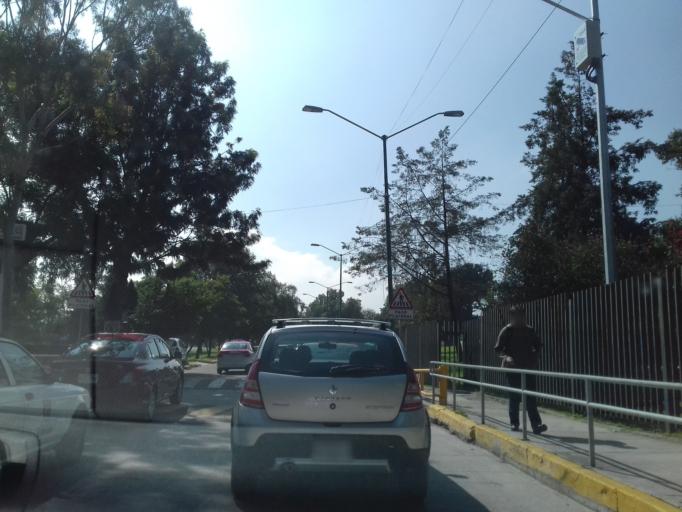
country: MX
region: Mexico City
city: Magdalena Contreras
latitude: 19.3319
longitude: -99.1958
